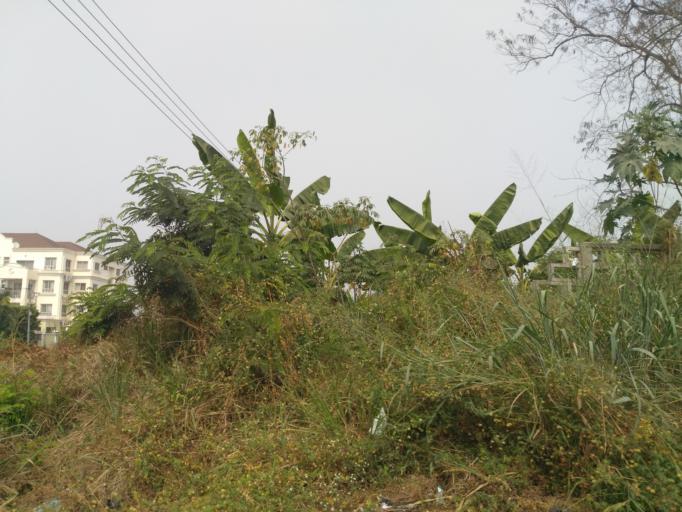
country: GH
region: Ashanti
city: Kumasi
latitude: 6.6753
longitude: -1.6319
